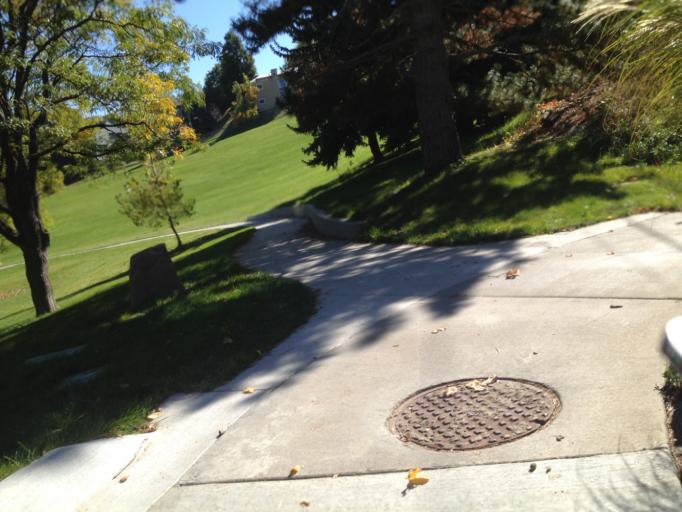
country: US
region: Colorado
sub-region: Boulder County
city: Boulder
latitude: 39.9798
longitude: -105.2411
